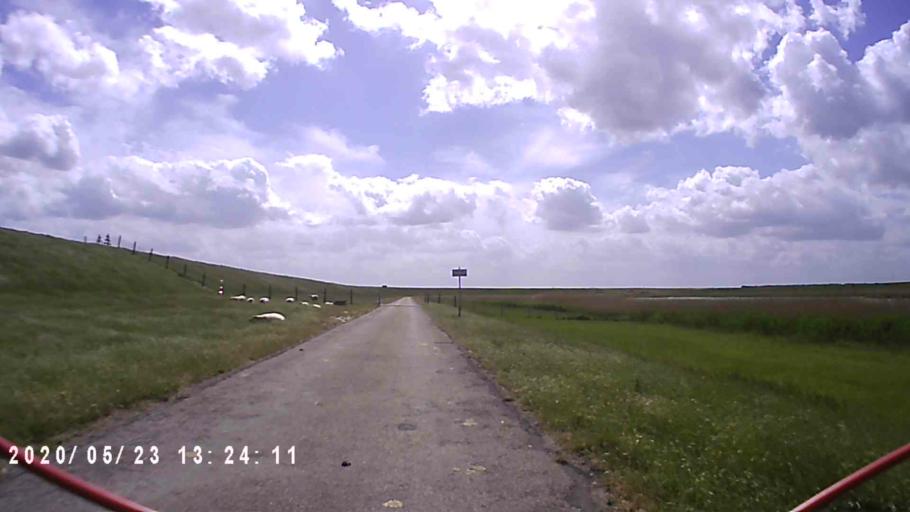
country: NL
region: Groningen
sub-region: Gemeente  Oldambt
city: Winschoten
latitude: 53.2844
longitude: 7.0834
